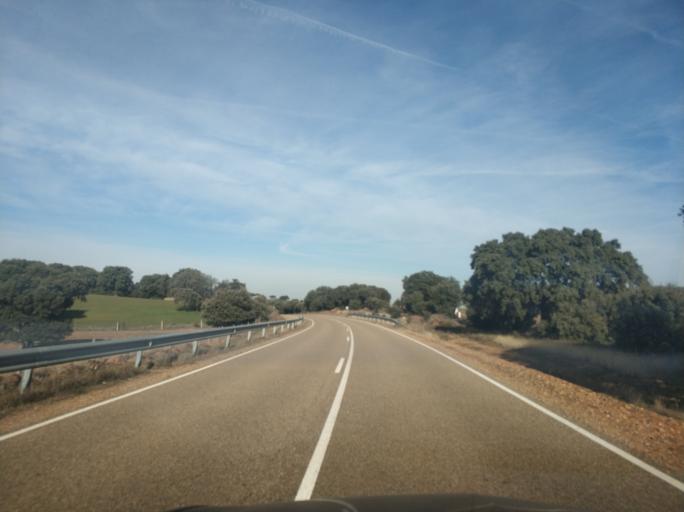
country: ES
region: Castille and Leon
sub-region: Provincia de Salamanca
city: Zarapicos
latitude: 41.0038
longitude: -5.8315
